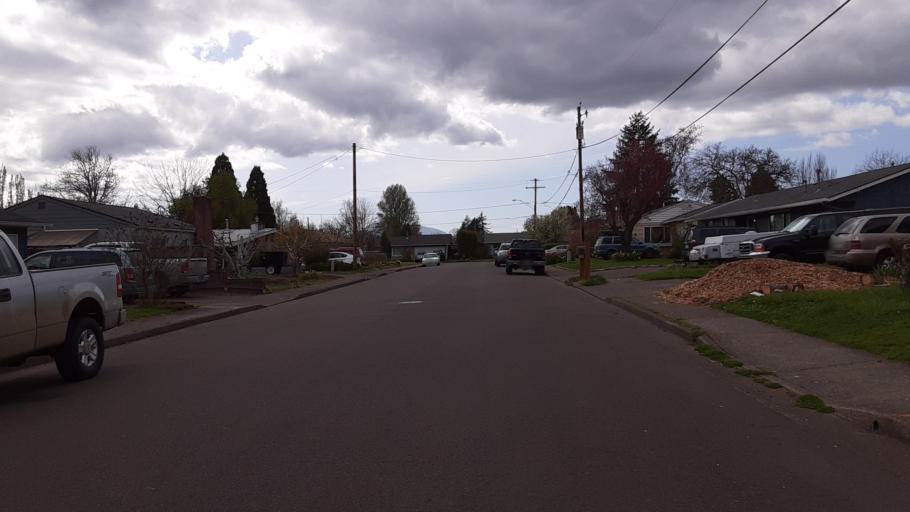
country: US
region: Oregon
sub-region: Benton County
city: Corvallis
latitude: 44.5397
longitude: -123.2591
